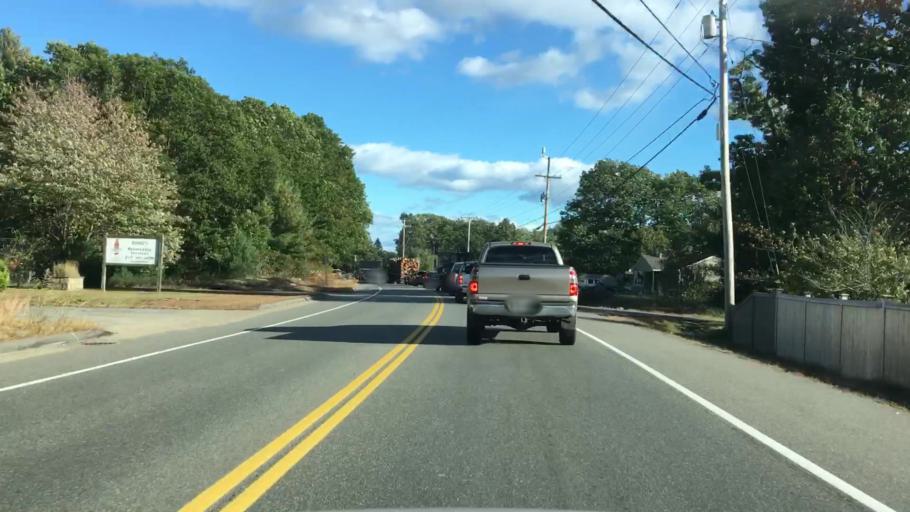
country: US
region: Maine
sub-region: York County
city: Wells Beach Station
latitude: 43.3248
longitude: -70.6151
